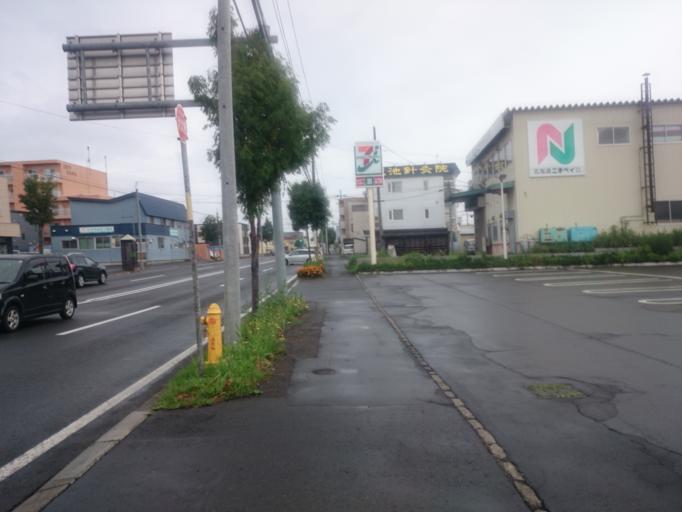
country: JP
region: Hokkaido
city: Sapporo
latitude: 43.0565
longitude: 141.4040
